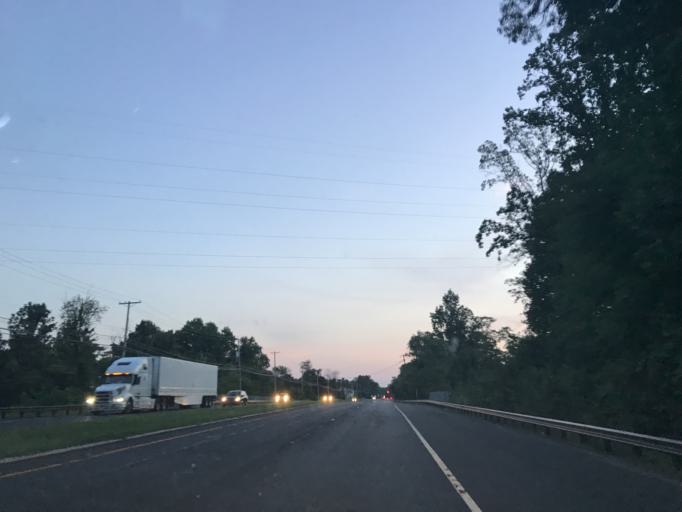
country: US
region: New Jersey
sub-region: Burlington County
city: Roebling
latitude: 40.1165
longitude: -74.7589
